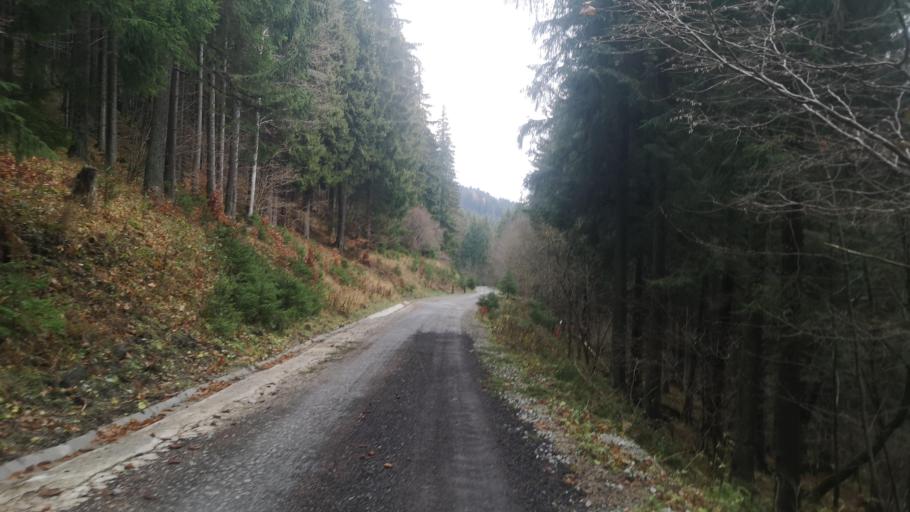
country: SK
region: Banskobystricky
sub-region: Okres Ziar nad Hronom
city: Kremnica
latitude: 48.7695
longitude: 18.9546
